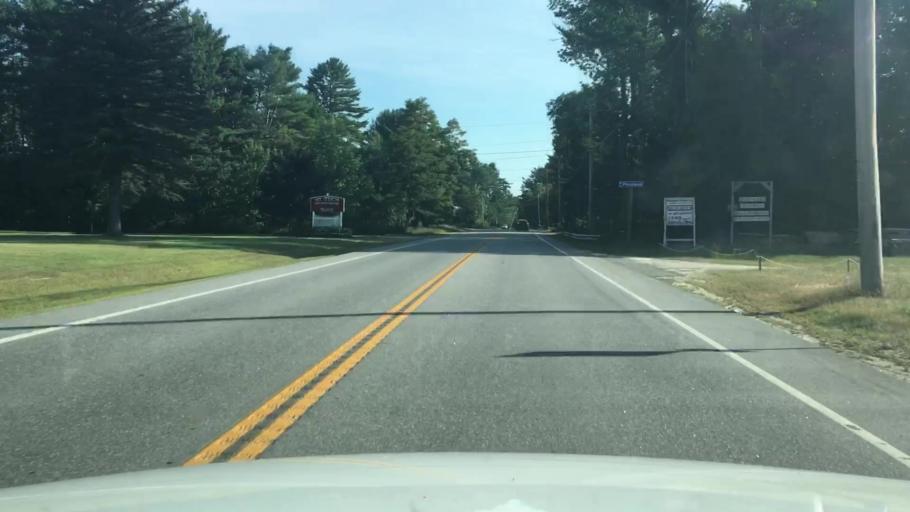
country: US
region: Maine
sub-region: Cumberland County
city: New Gloucester
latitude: 43.9293
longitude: -70.3099
